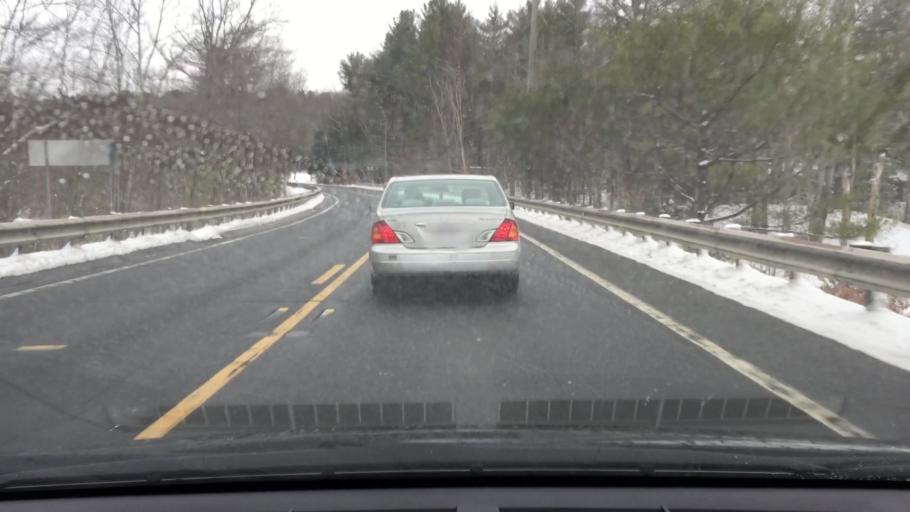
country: US
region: Massachusetts
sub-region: Hampshire County
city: Pelham
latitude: 42.3490
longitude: -72.4041
